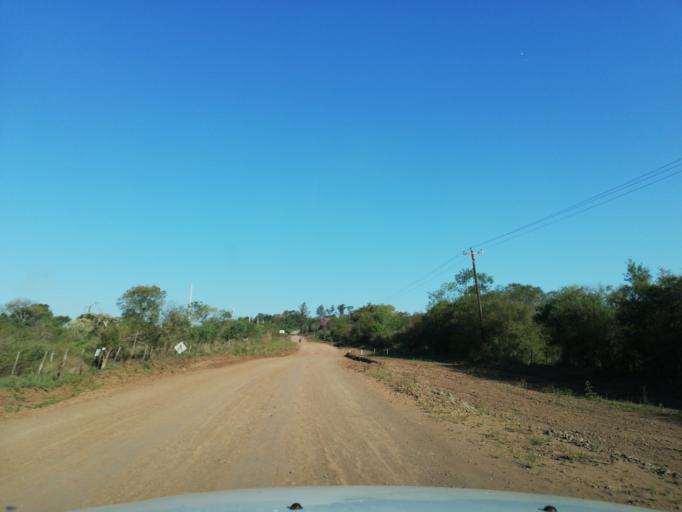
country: AR
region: Misiones
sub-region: Departamento de Candelaria
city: Candelaria
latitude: -27.5371
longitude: -55.7160
